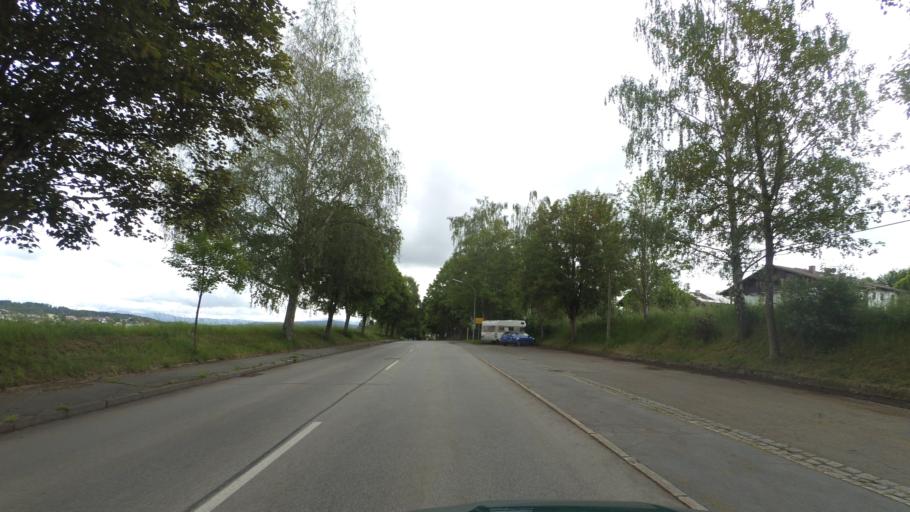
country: DE
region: Bavaria
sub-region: Lower Bavaria
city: Regen
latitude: 48.9723
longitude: 13.1141
